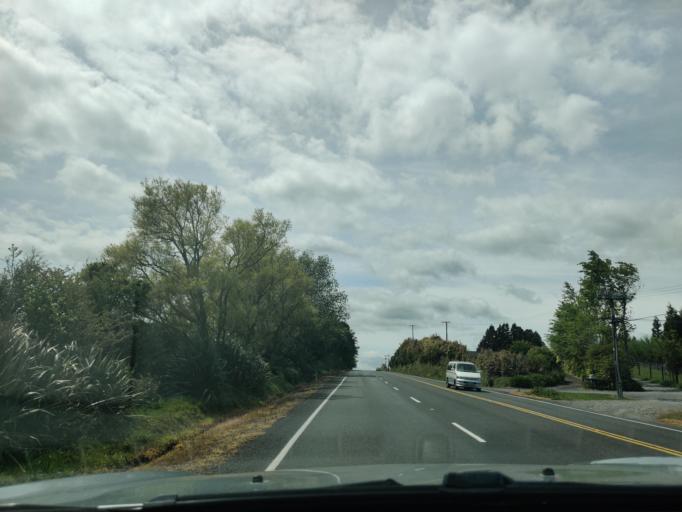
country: NZ
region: Taranaki
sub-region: New Plymouth District
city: New Plymouth
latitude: -39.1511
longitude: 174.1632
